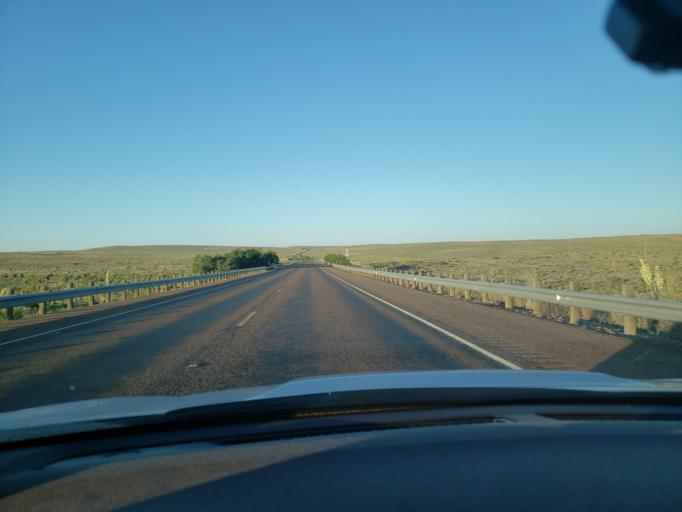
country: US
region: Texas
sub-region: El Paso County
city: Homestead Meadows South
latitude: 31.8281
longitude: -105.8746
